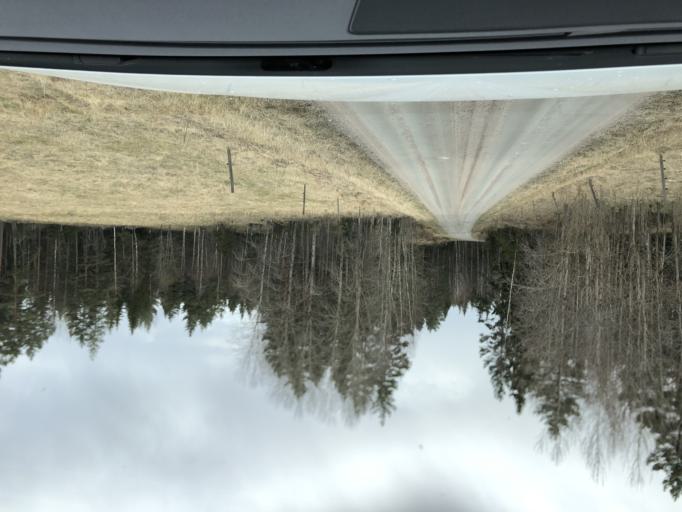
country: SE
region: Gaevleborg
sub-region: Gavle Kommun
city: Hedesunda
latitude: 60.3176
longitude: 17.1054
